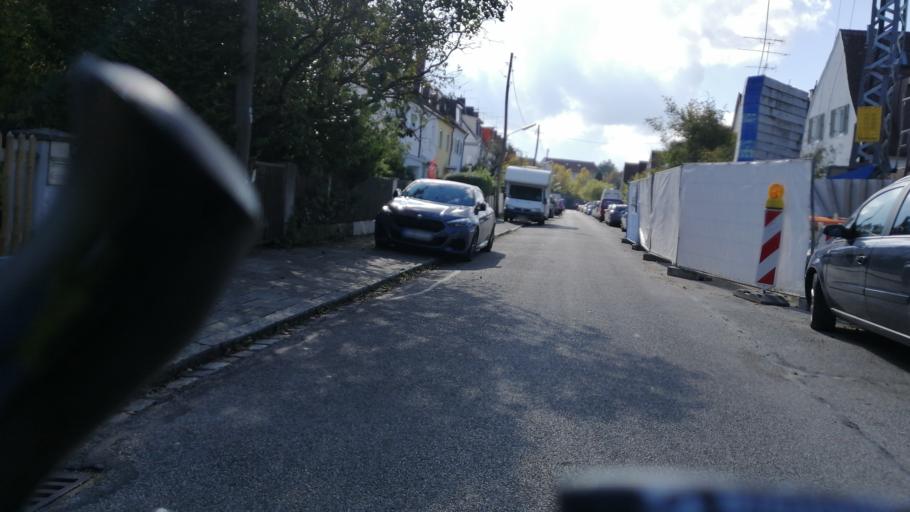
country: DE
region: Bavaria
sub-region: Upper Bavaria
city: Pasing
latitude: 48.1312
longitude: 11.4934
